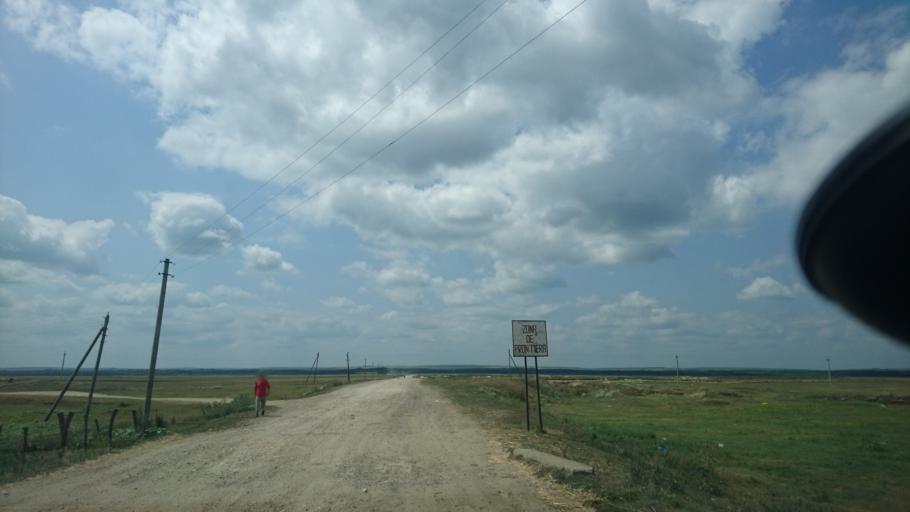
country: RO
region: Iasi
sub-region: Comuna Bivolari
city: Bivolari
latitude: 47.5607
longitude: 27.4850
